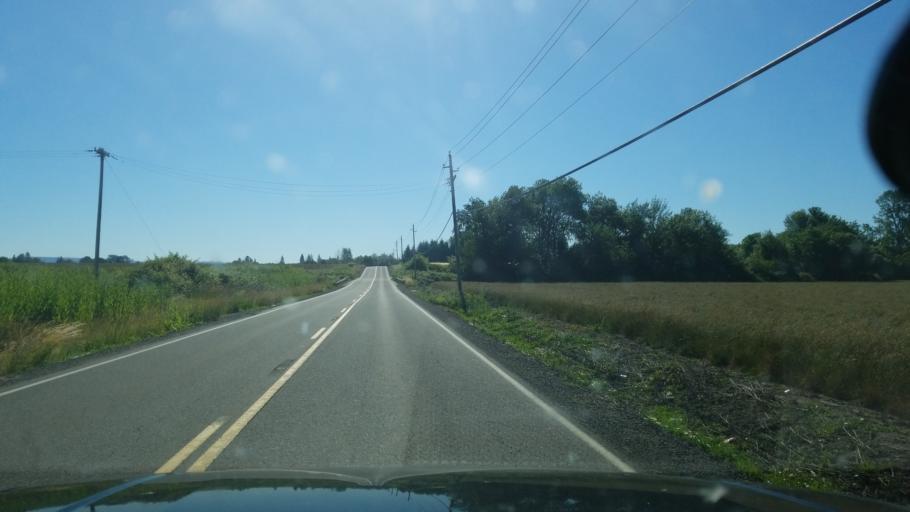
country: US
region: Oregon
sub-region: Yamhill County
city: McMinnville
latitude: 45.2305
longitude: -123.2386
